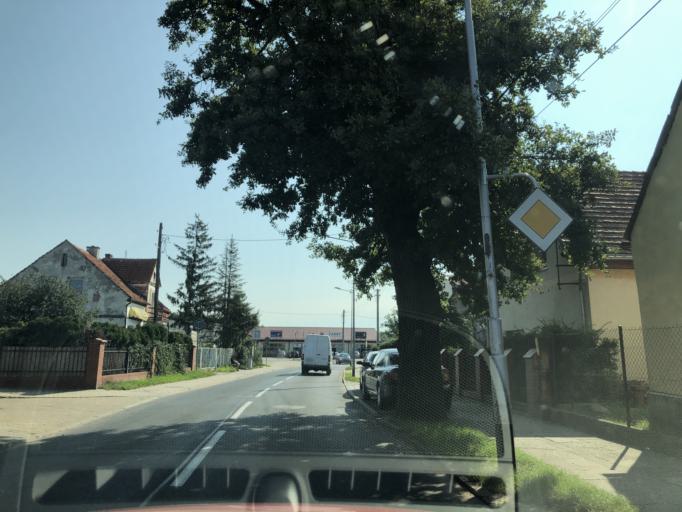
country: PL
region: Lower Silesian Voivodeship
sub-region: Powiat wroclawski
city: Smolec
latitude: 51.1736
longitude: 16.9122
